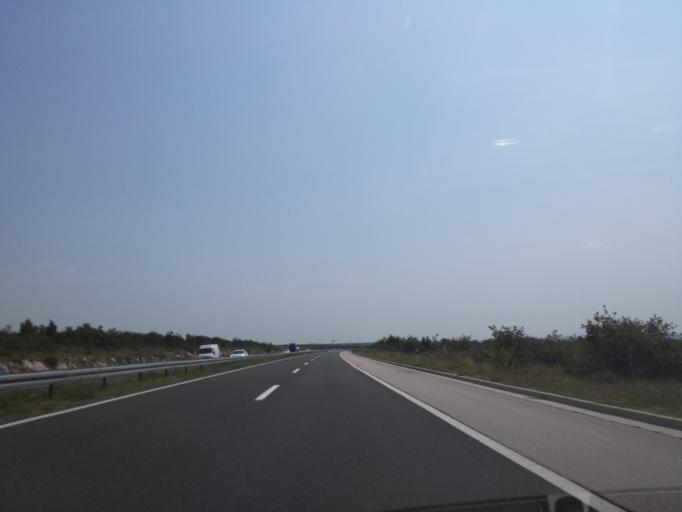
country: HR
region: Zadarska
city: Polaca
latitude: 44.0356
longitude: 15.5603
